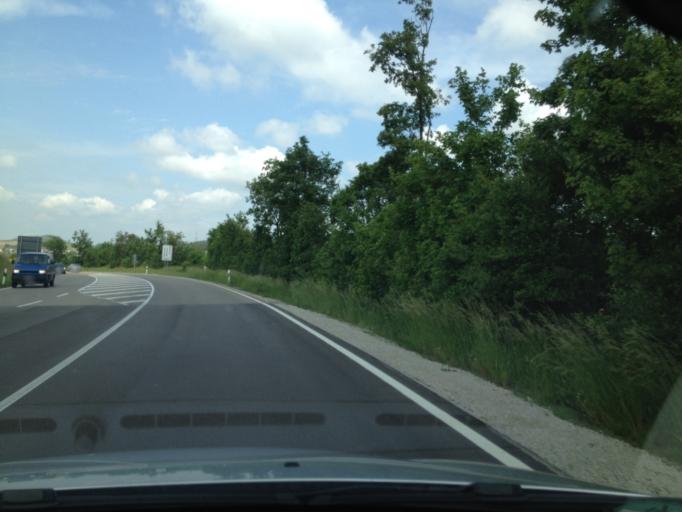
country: DE
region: Bavaria
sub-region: Swabia
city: Harburg
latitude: 48.7895
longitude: 10.6856
